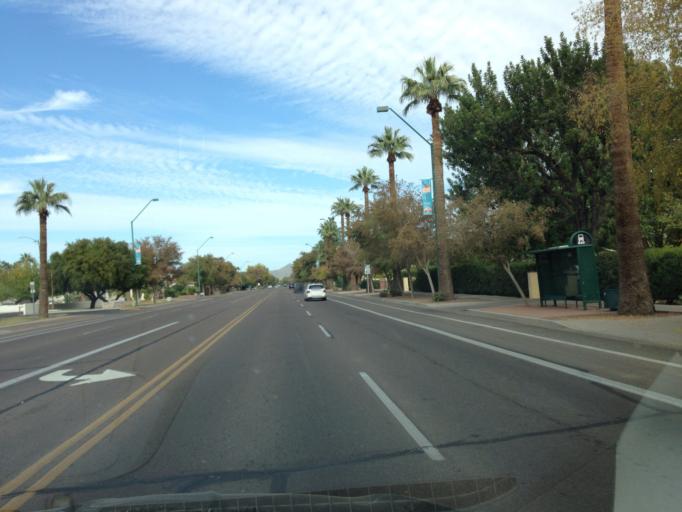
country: US
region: Arizona
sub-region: Maricopa County
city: Phoenix
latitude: 33.5168
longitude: -112.0737
